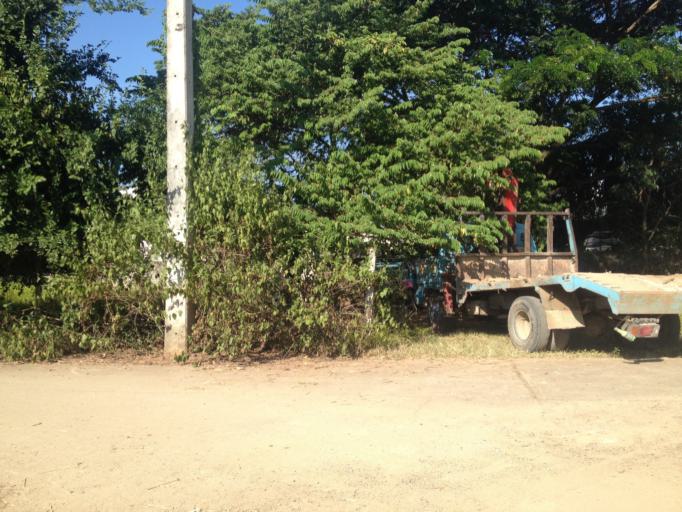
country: TH
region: Chiang Mai
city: Hang Dong
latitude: 18.7017
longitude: 98.9252
